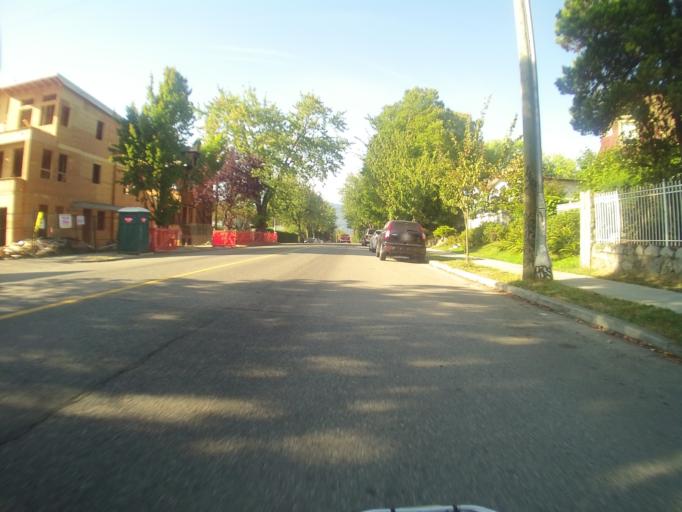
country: CA
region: British Columbia
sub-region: Fraser Valley Regional District
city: North Vancouver
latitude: 49.2752
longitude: -123.0656
